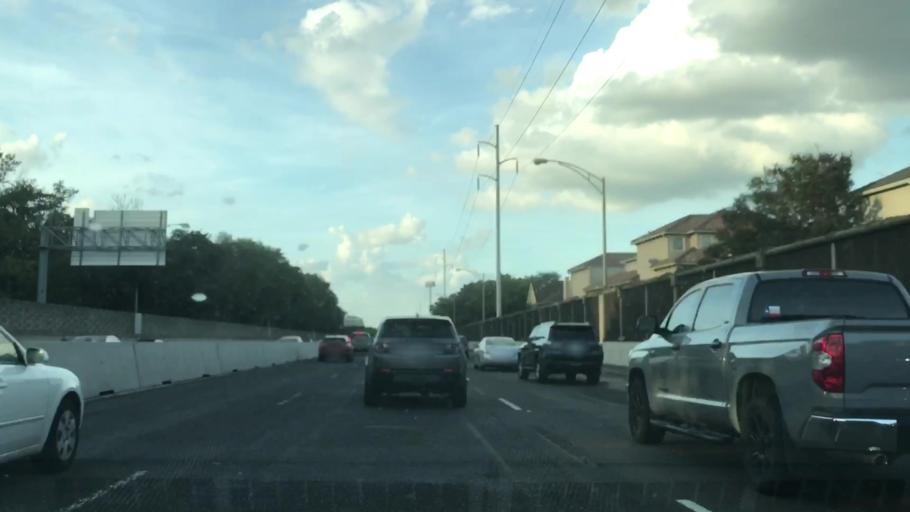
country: US
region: Texas
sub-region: Dallas County
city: University Park
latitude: 32.8394
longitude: -96.8146
